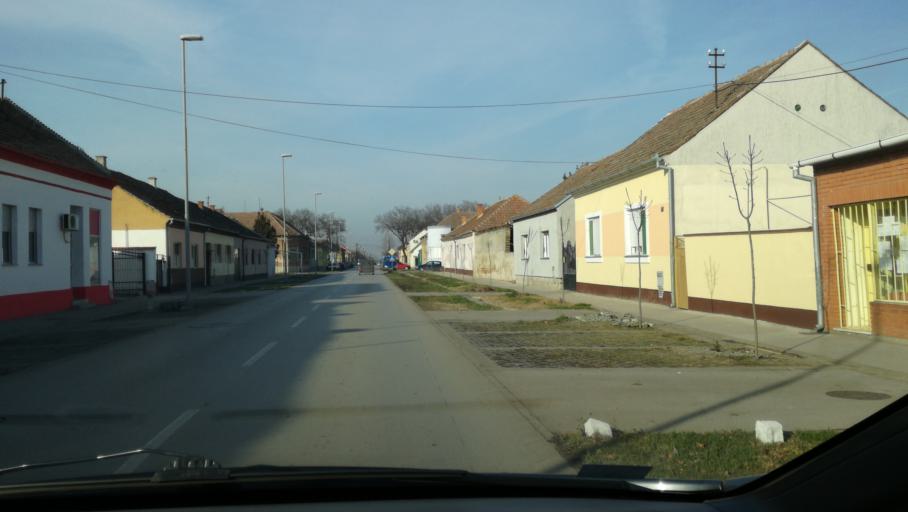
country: RS
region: Autonomna Pokrajina Vojvodina
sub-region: Severnobanatski Okrug
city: Kikinda
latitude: 45.8351
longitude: 20.4785
